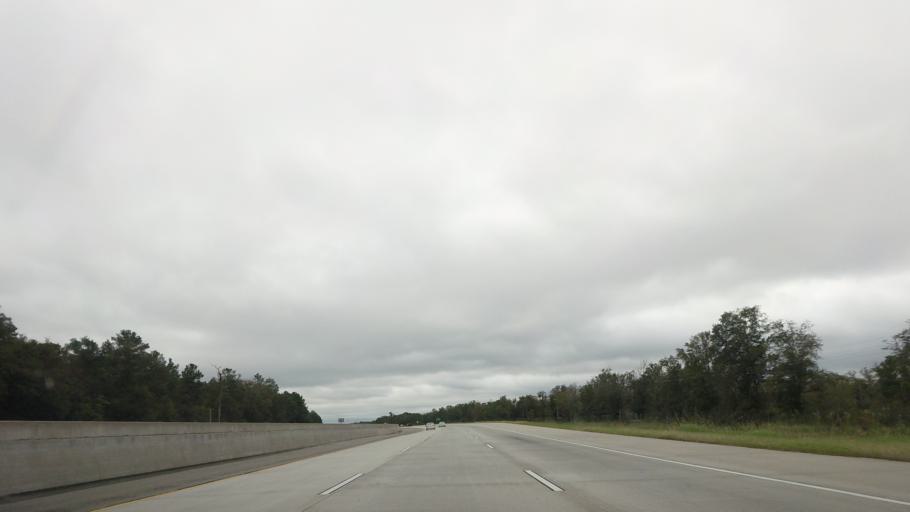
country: US
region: Georgia
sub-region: Lowndes County
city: Hahira
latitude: 31.0323
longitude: -83.3983
